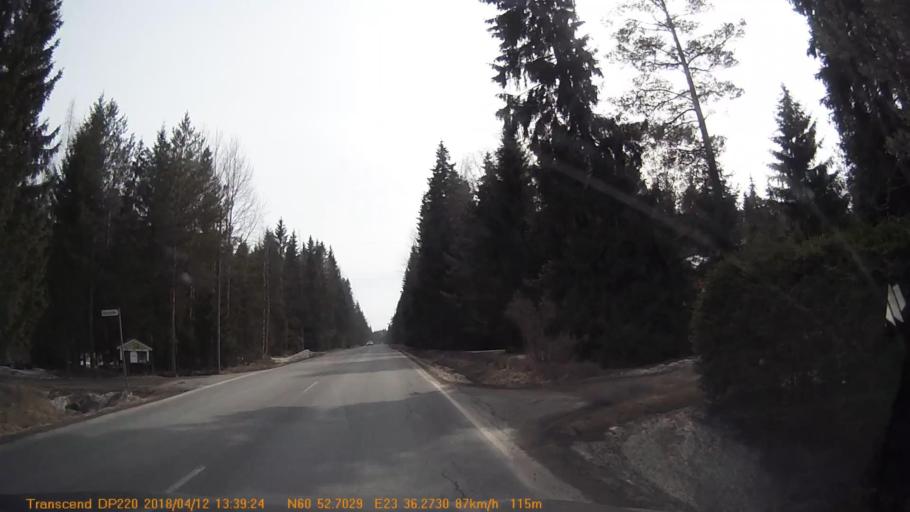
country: FI
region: Haeme
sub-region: Forssa
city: Forssa
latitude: 60.8781
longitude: 23.6047
